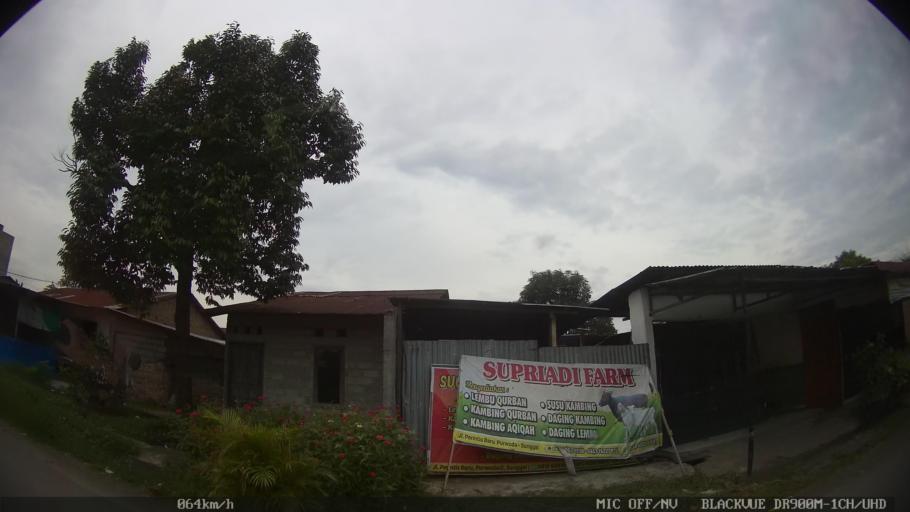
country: ID
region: North Sumatra
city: Sunggal
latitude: 3.6138
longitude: 98.5959
